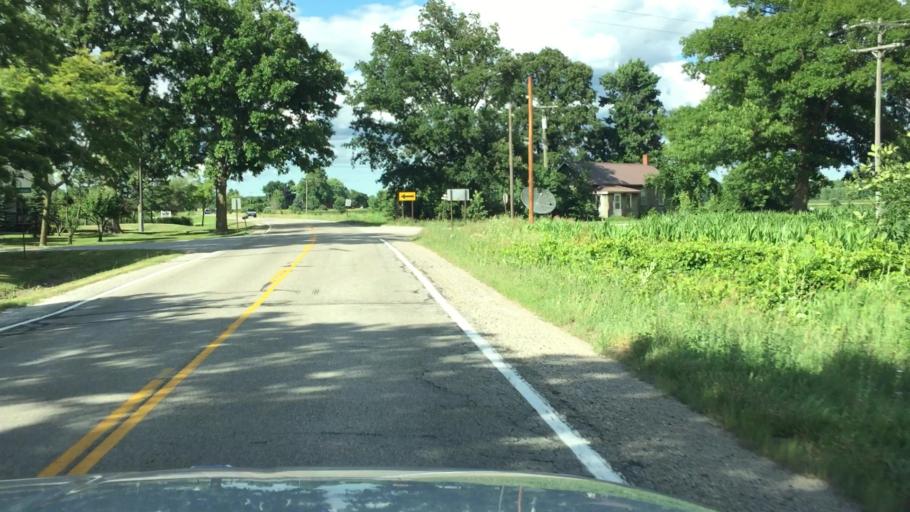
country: US
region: Michigan
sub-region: Saint Clair County
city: Capac
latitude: 43.0838
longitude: -82.9139
